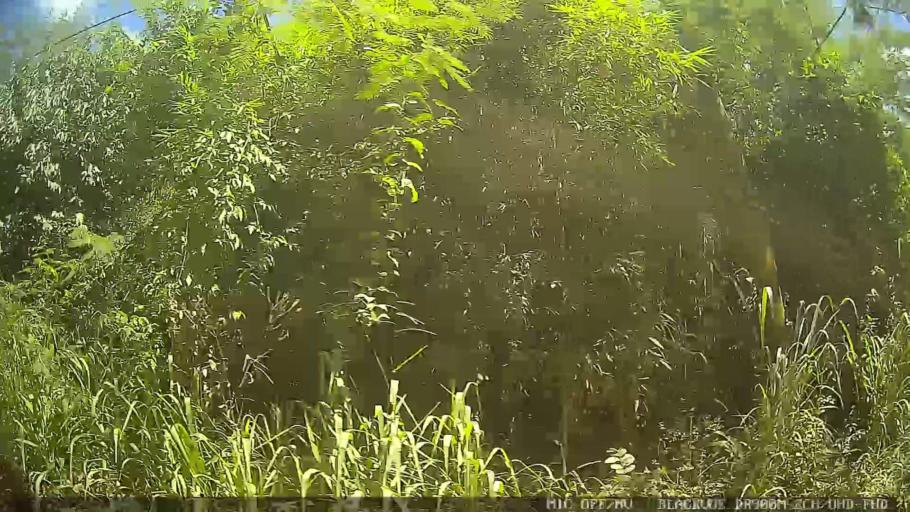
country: BR
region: Sao Paulo
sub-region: Atibaia
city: Atibaia
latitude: -23.1489
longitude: -46.6041
